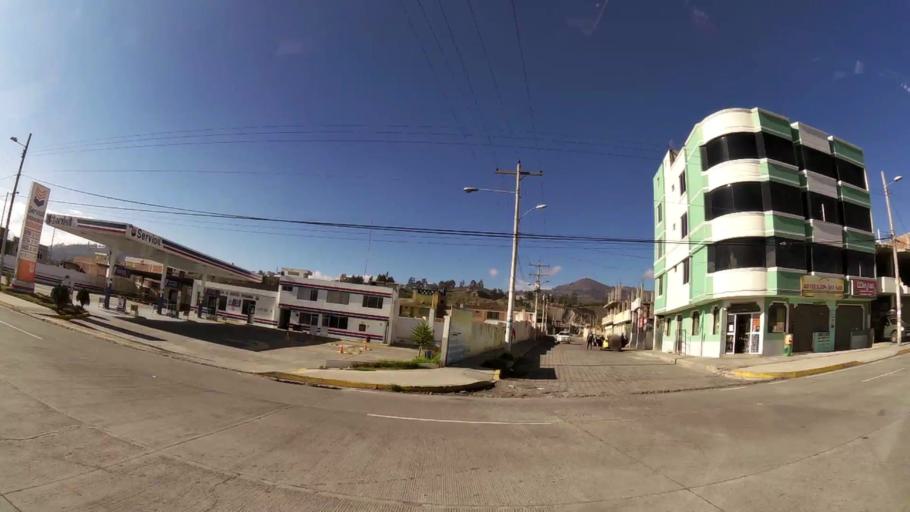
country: EC
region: Chimborazo
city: Riobamba
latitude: -1.6573
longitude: -78.6909
